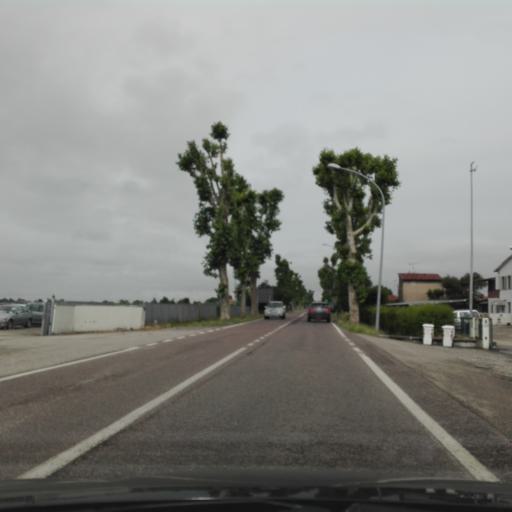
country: IT
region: Veneto
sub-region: Provincia di Rovigo
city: Rovigo
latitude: 45.0773
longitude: 11.7650
